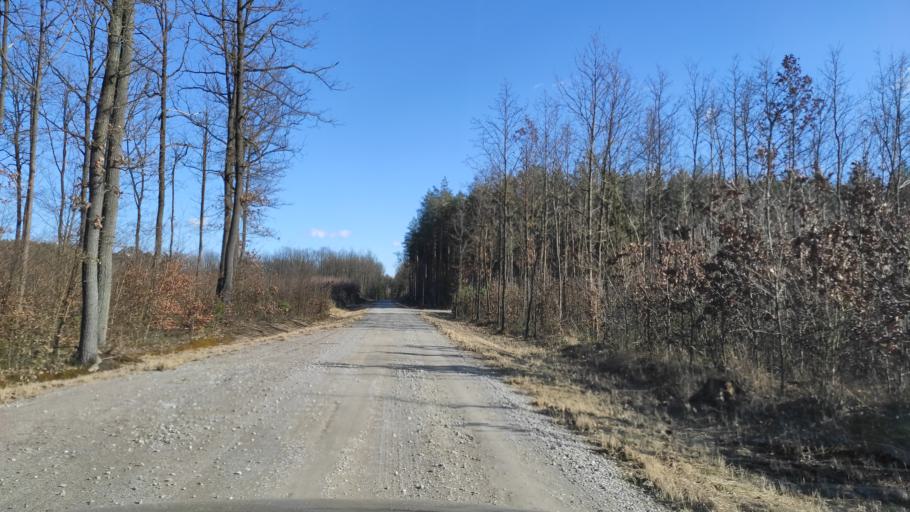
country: PL
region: Masovian Voivodeship
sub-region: Powiat radomski
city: Jedlnia-Letnisko
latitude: 51.4508
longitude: 21.2876
